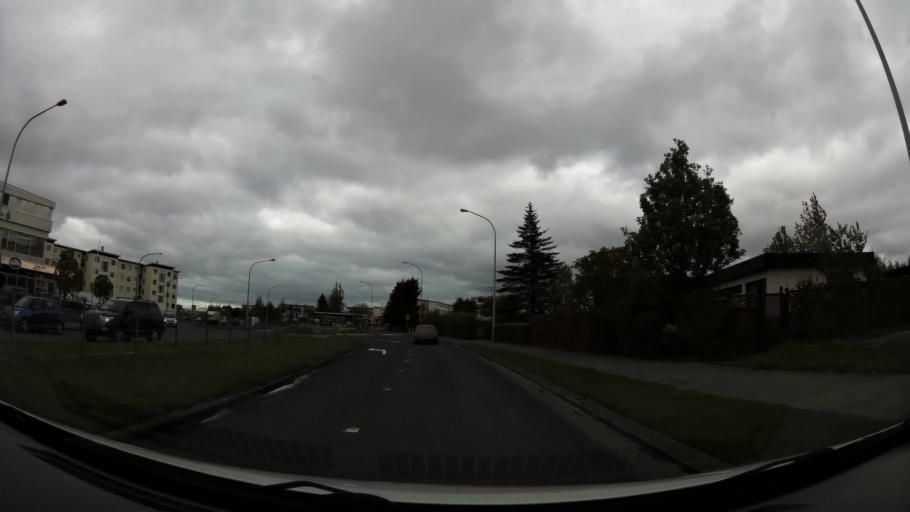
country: IS
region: Capital Region
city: Reykjavik
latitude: 64.1326
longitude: -21.8825
